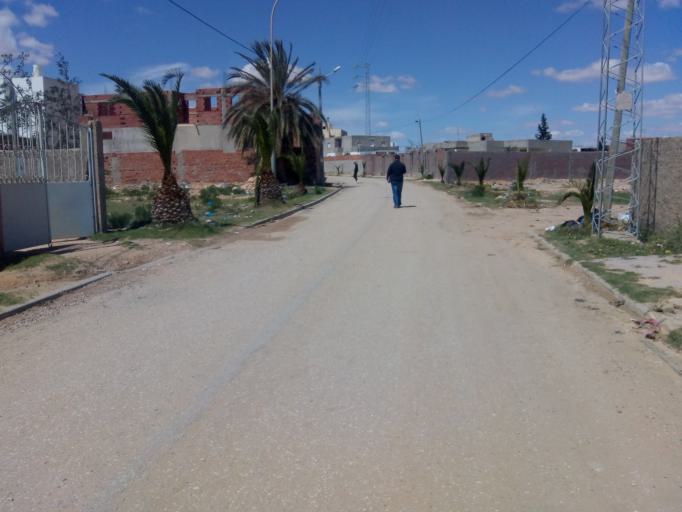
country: TN
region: Safaqis
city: Sfax
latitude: 34.7425
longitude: 10.5301
